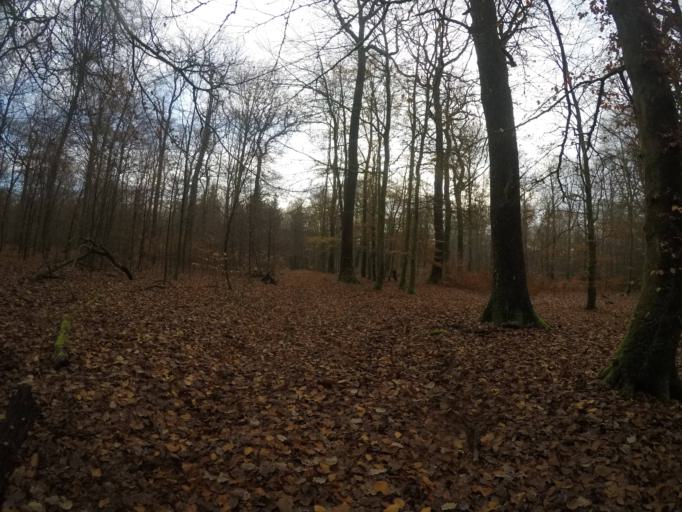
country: BE
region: Wallonia
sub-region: Province du Luxembourg
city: Habay-la-Vieille
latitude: 49.7432
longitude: 5.5984
